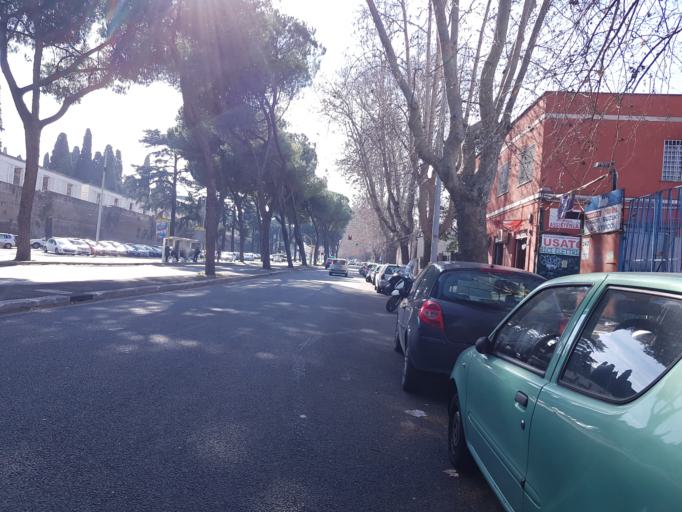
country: IT
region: Latium
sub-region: Citta metropolitana di Roma Capitale
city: Rome
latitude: 41.9066
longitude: 12.5230
